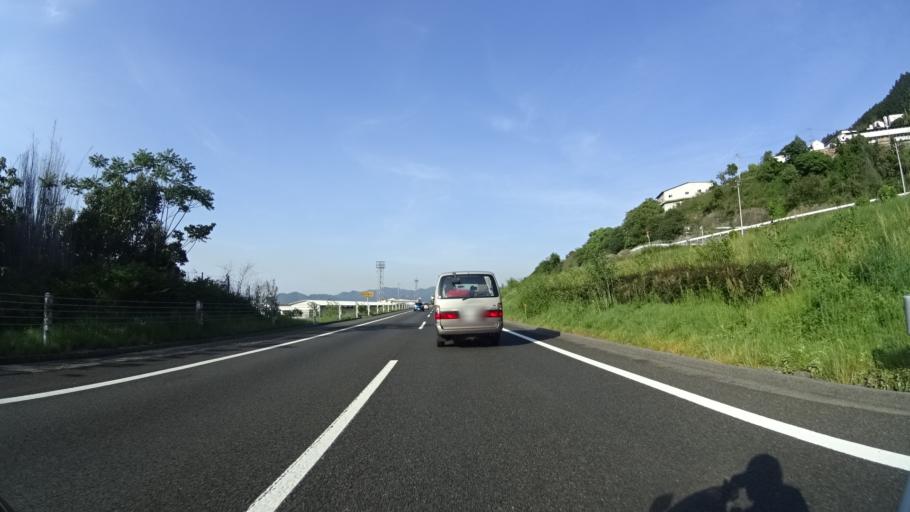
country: JP
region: Ehime
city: Kawanoecho
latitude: 33.9660
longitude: 133.5408
